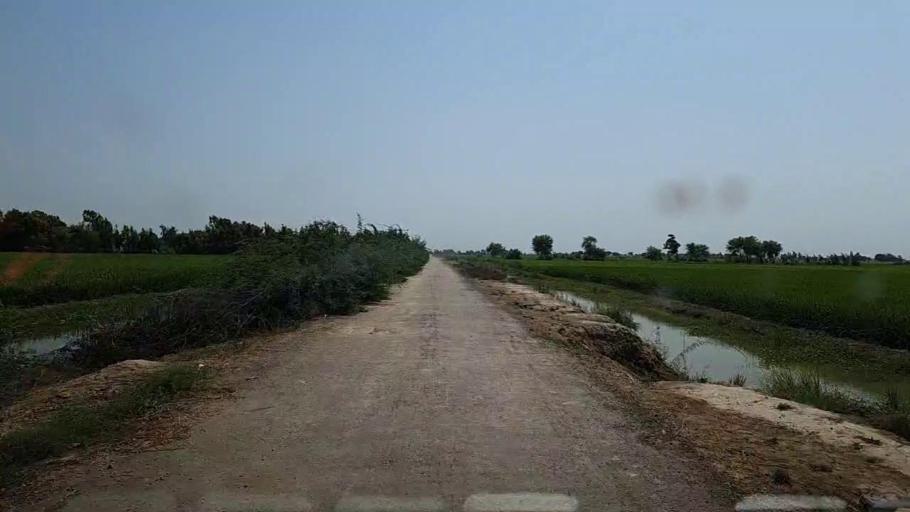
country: PK
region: Sindh
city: Mirpur Batoro
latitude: 24.6126
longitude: 68.4523
